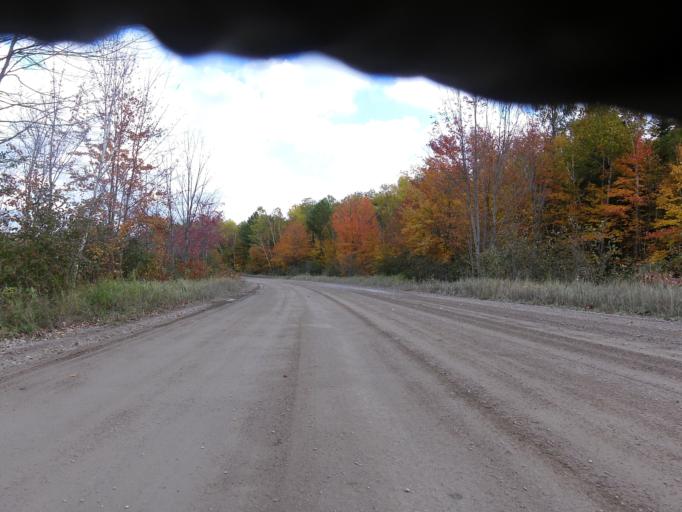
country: CA
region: Ontario
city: Petawawa
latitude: 45.8092
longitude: -77.3683
